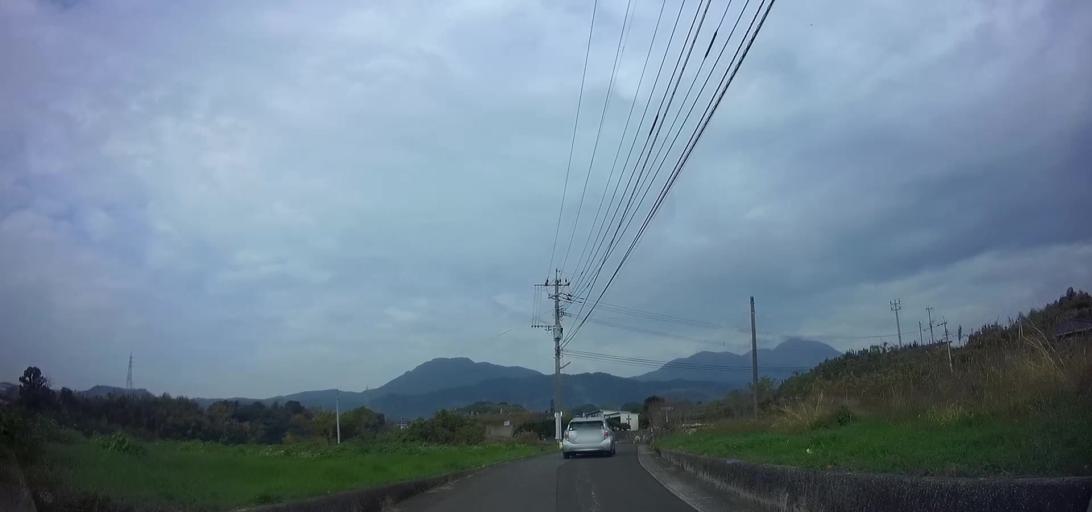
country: JP
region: Nagasaki
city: Shimabara
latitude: 32.6784
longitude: 130.3001
